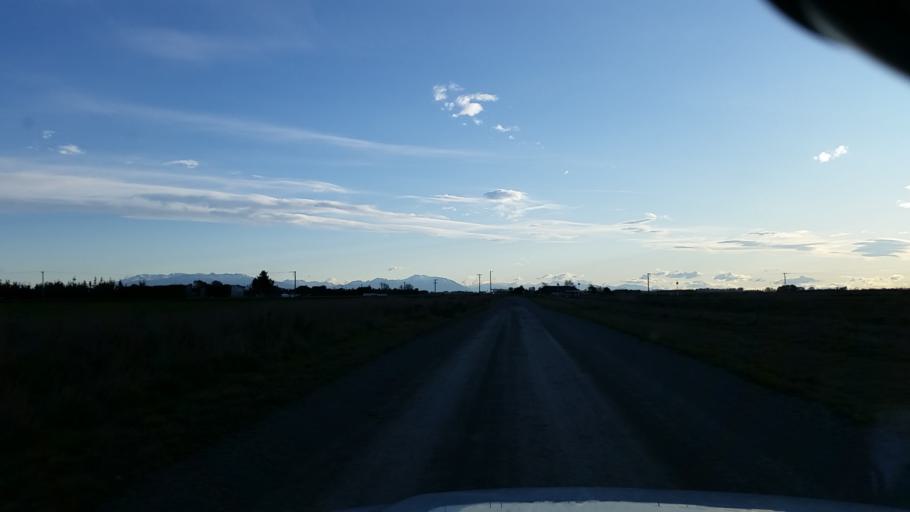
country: NZ
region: Canterbury
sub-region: Ashburton District
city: Tinwald
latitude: -43.9782
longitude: 171.5080
